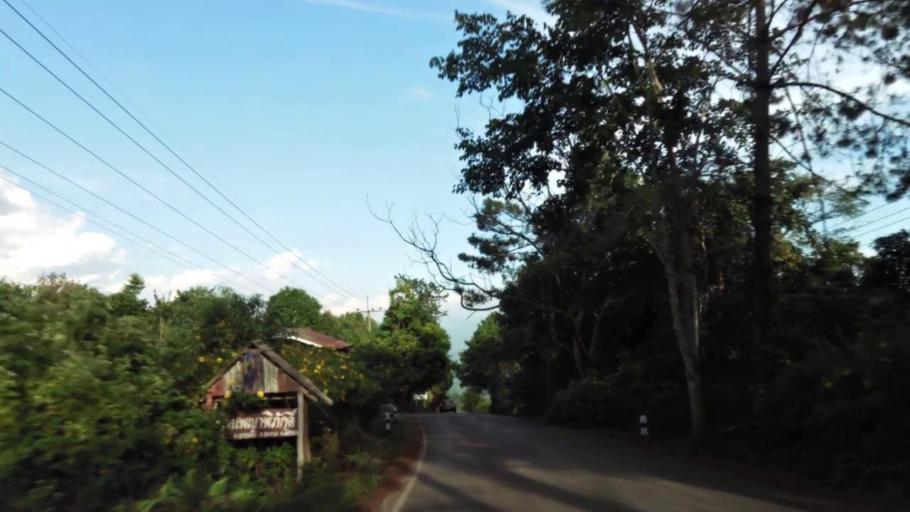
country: TH
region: Chiang Rai
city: Khun Tan
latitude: 19.8670
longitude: 100.3383
